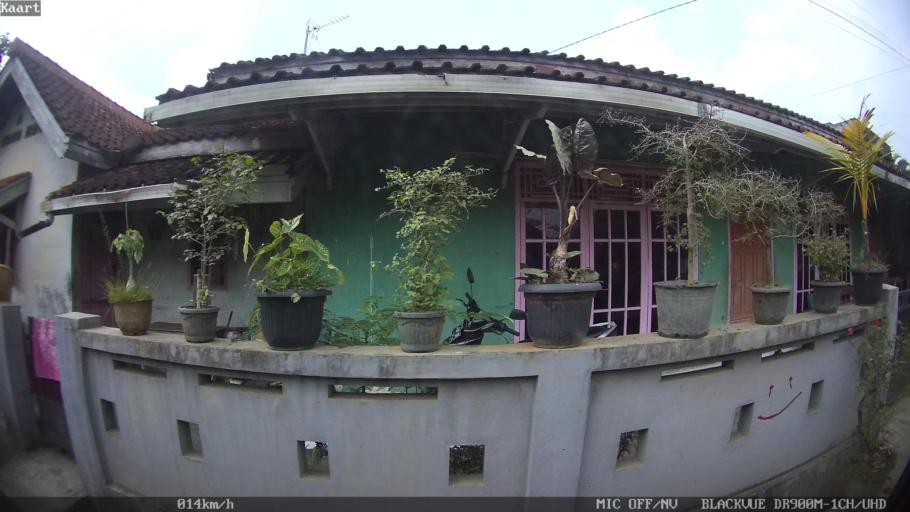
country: ID
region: Lampung
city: Gadingrejo
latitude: -5.3712
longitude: 105.0616
